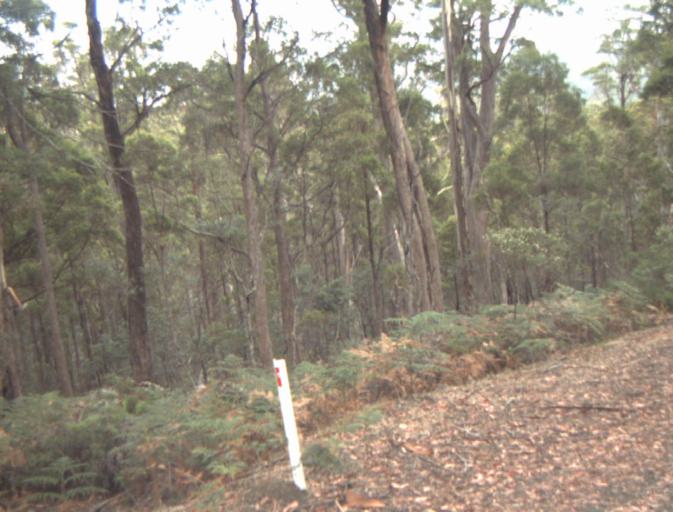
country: AU
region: Tasmania
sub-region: Northern Midlands
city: Evandale
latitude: -41.4910
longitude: 147.5464
